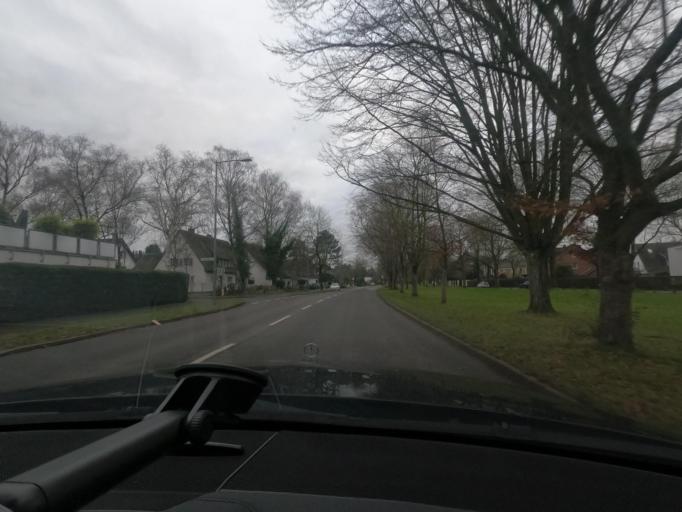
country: DE
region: North Rhine-Westphalia
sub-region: Regierungsbezirk Dusseldorf
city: Krefeld
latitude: 51.3504
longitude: 6.5926
